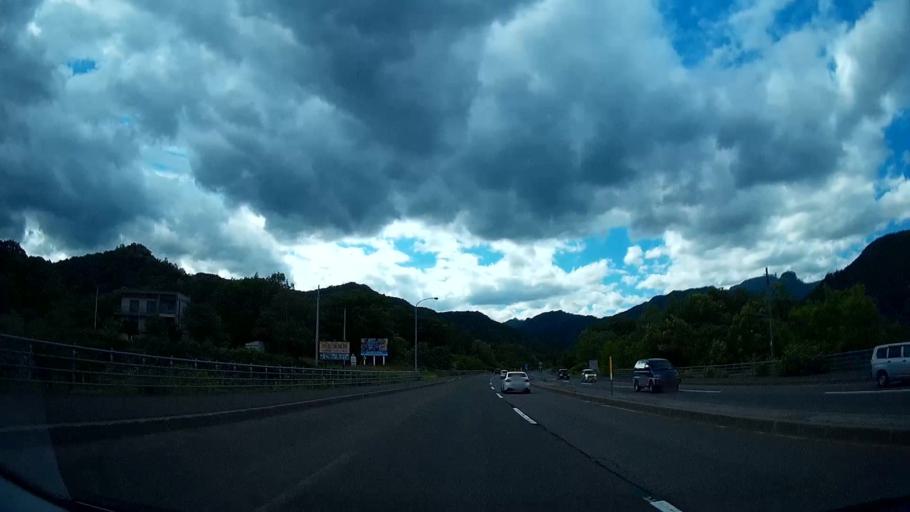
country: JP
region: Hokkaido
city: Sapporo
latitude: 42.9578
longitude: 141.2298
